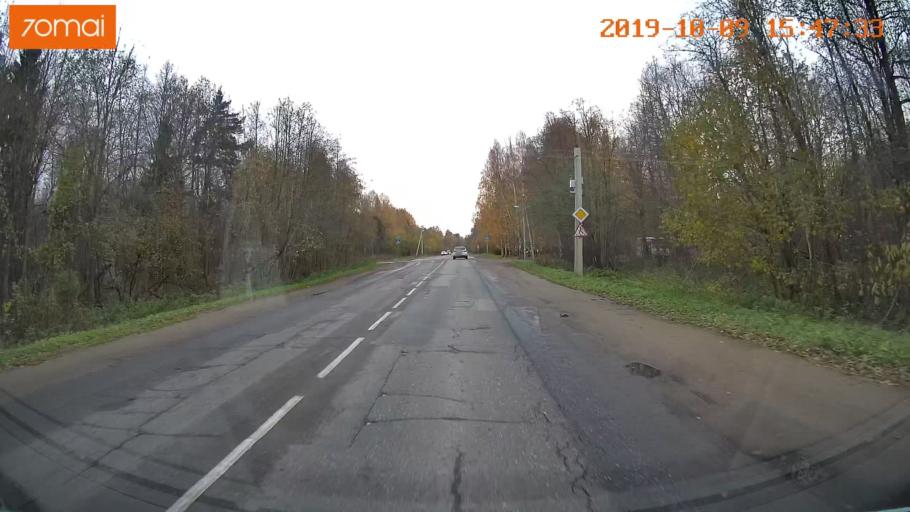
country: RU
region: Kostroma
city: Oktyabr'skiy
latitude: 57.8167
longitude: 41.0271
